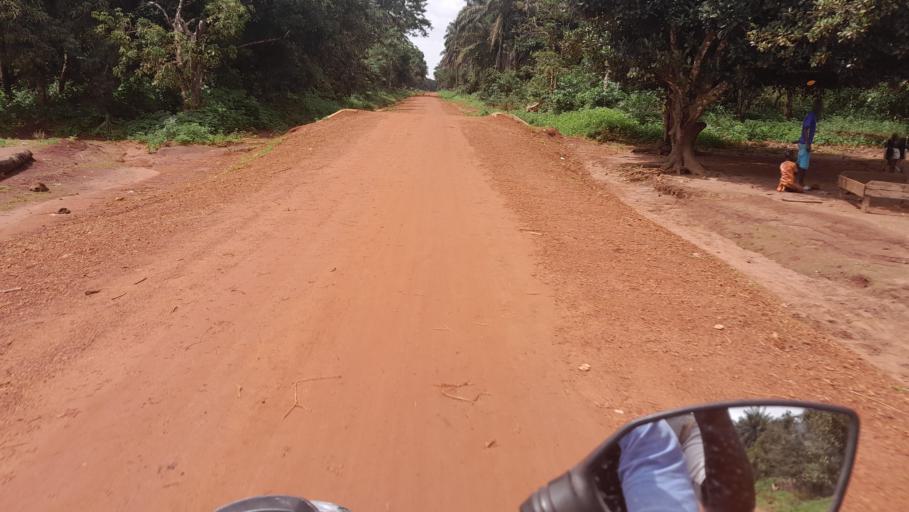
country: GN
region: Boke
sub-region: Boffa
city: Boffa
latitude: 10.0178
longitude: -13.8889
